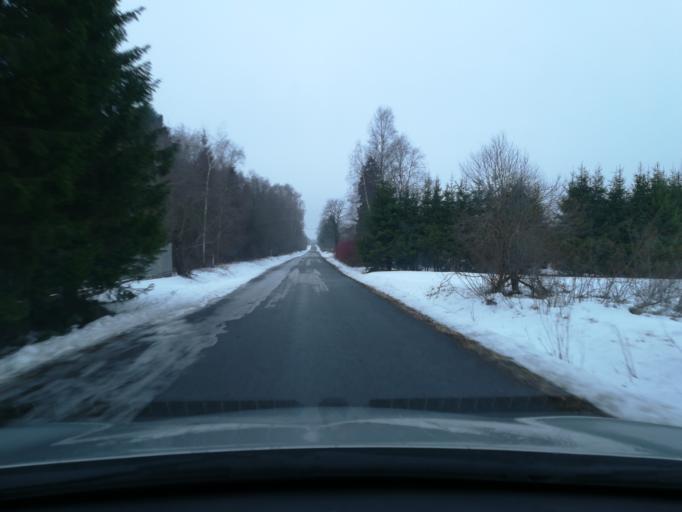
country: EE
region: Harju
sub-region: Raasiku vald
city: Raasiku
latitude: 59.3430
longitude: 25.2467
